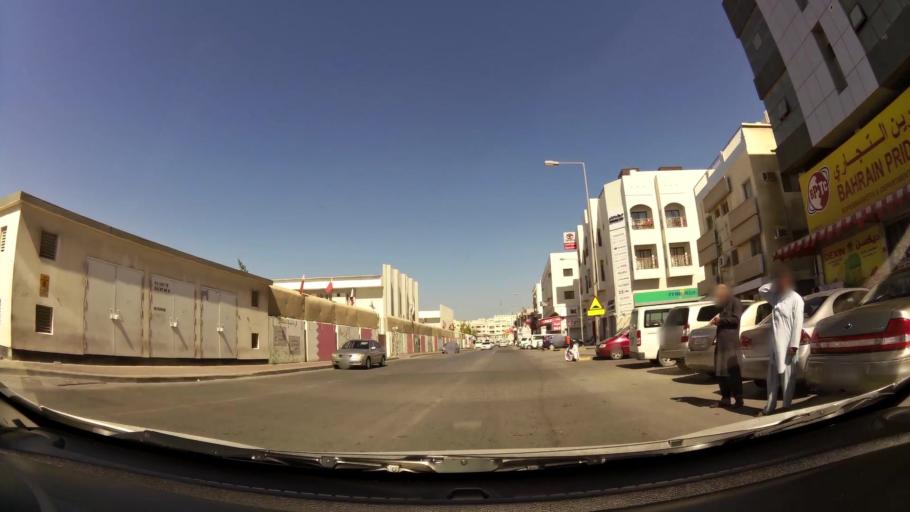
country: BH
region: Muharraq
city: Al Muharraq
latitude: 26.2460
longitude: 50.6107
